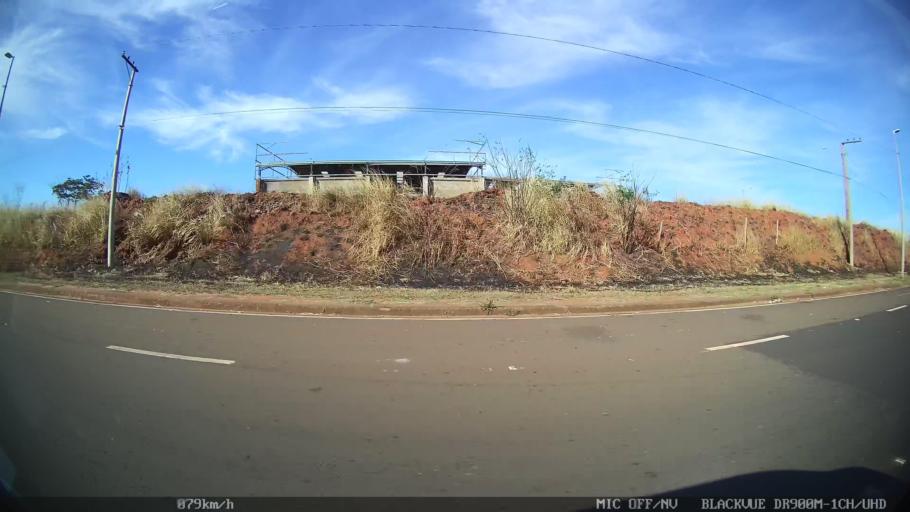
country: BR
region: Sao Paulo
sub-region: Sao Jose Do Rio Preto
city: Sao Jose do Rio Preto
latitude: -20.7378
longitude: -49.3377
